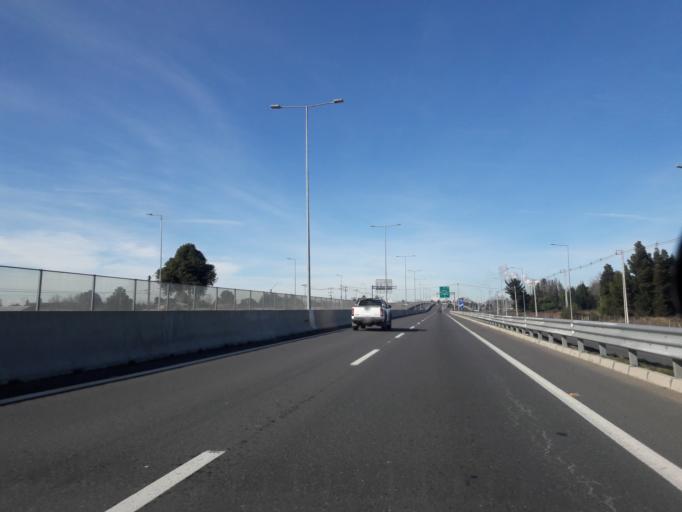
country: CL
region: Biobio
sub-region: Provincia de Biobio
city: Cabrero
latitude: -37.0366
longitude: -72.4116
